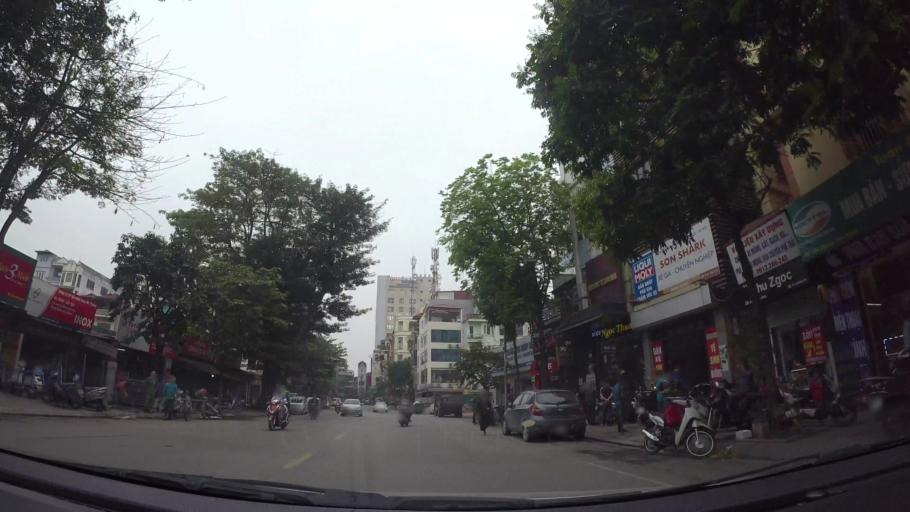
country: VN
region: Ha Noi
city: Dong Da
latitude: 21.0330
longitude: 105.8272
